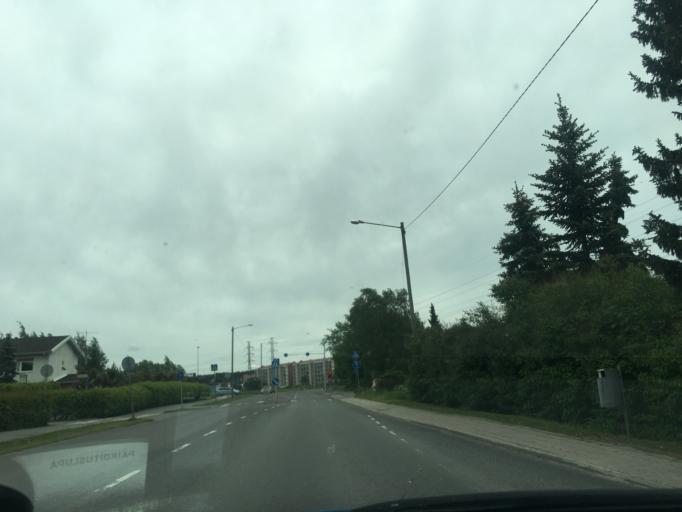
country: FI
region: Varsinais-Suomi
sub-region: Turku
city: Turku
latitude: 60.4725
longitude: 22.3058
